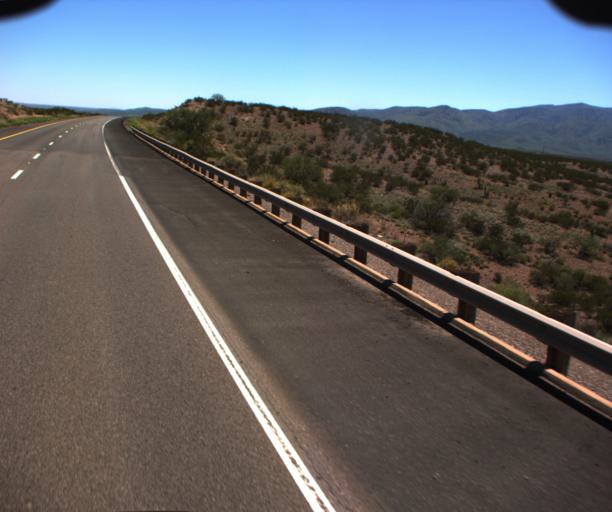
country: US
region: Arizona
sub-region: Greenlee County
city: Clifton
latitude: 33.0054
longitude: -109.2798
